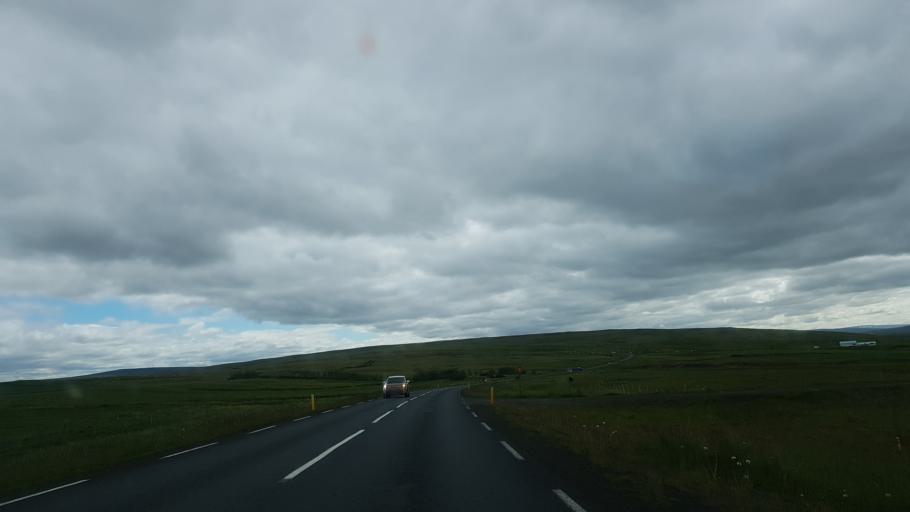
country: IS
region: Northwest
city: Saudarkrokur
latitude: 65.3621
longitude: -20.8941
